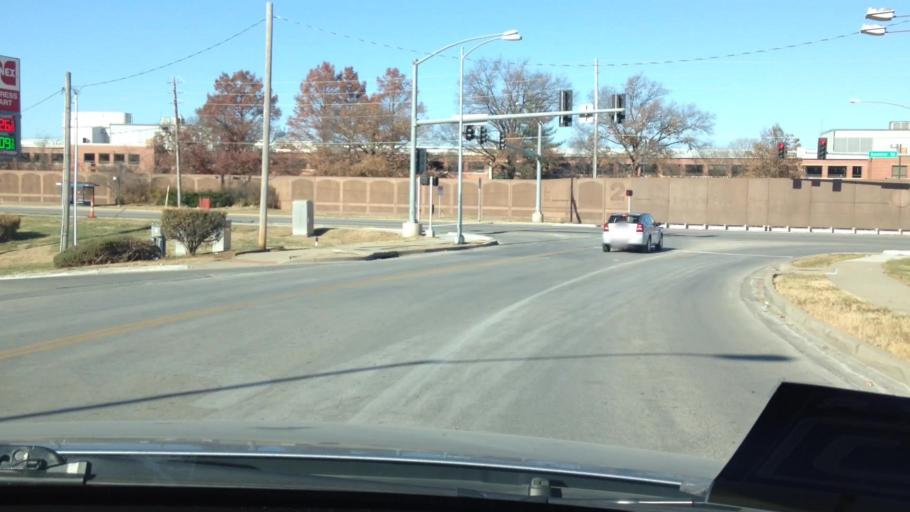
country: US
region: Kansas
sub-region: Johnson County
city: Leawood
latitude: 38.9546
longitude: -94.5726
